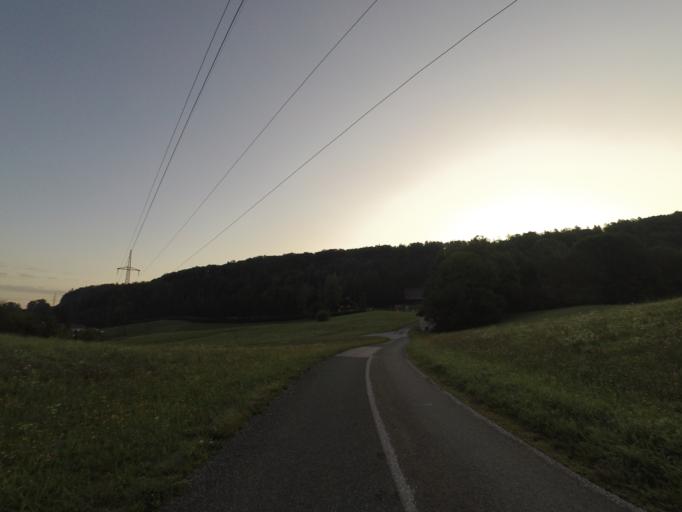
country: AT
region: Salzburg
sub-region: Politischer Bezirk Salzburg-Umgebung
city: Elsbethen
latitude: 47.7343
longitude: 13.0903
